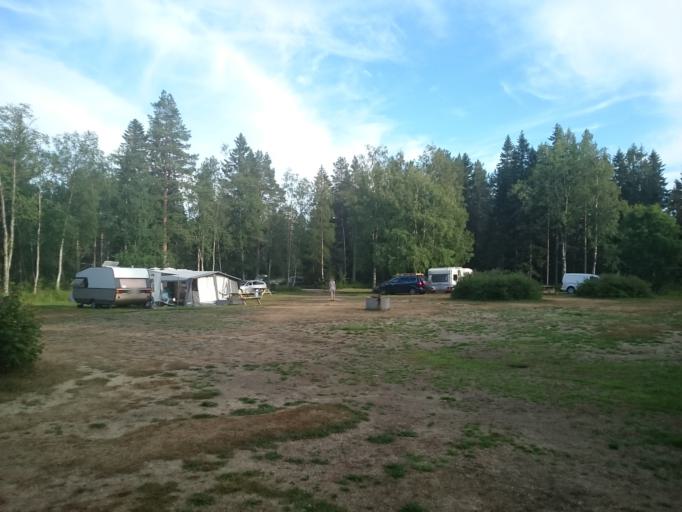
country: SE
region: Vaesterbotten
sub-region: Robertsfors Kommun
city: Robertsfors
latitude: 64.0025
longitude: 20.8921
